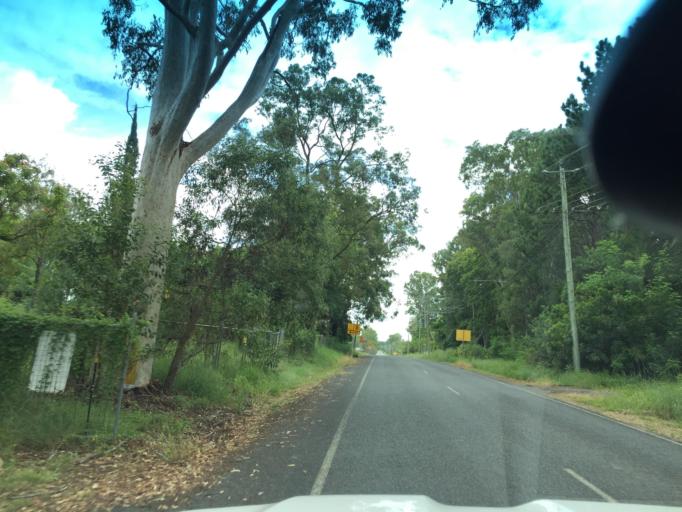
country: AU
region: Queensland
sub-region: Moreton Bay
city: Burpengary
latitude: -27.1665
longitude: 152.9889
